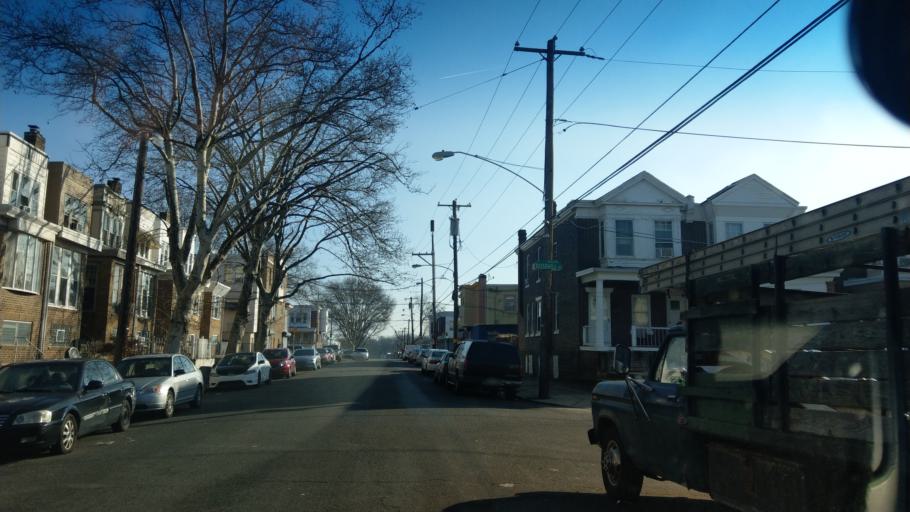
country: US
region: Pennsylvania
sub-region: Montgomery County
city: Rockledge
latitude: 40.0225
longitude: -75.1190
